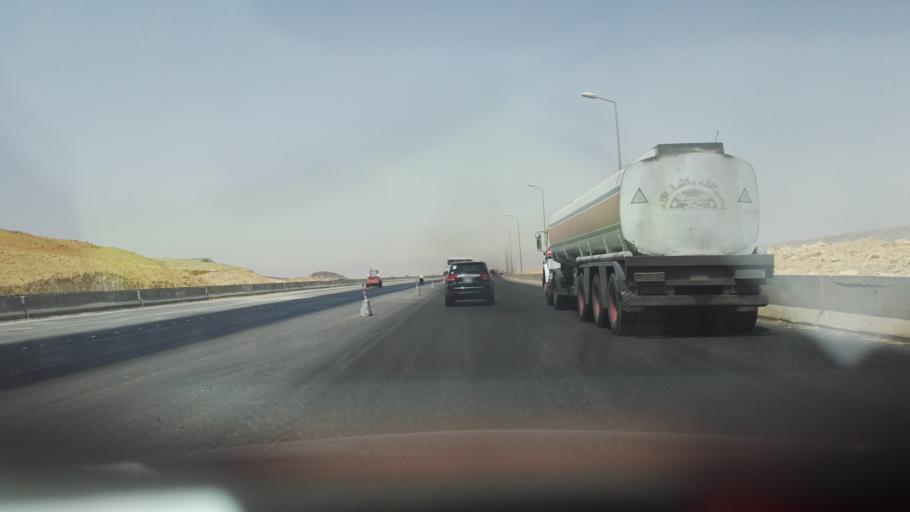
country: EG
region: As Suways
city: Ain Sukhna
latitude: 29.6990
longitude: 32.1020
